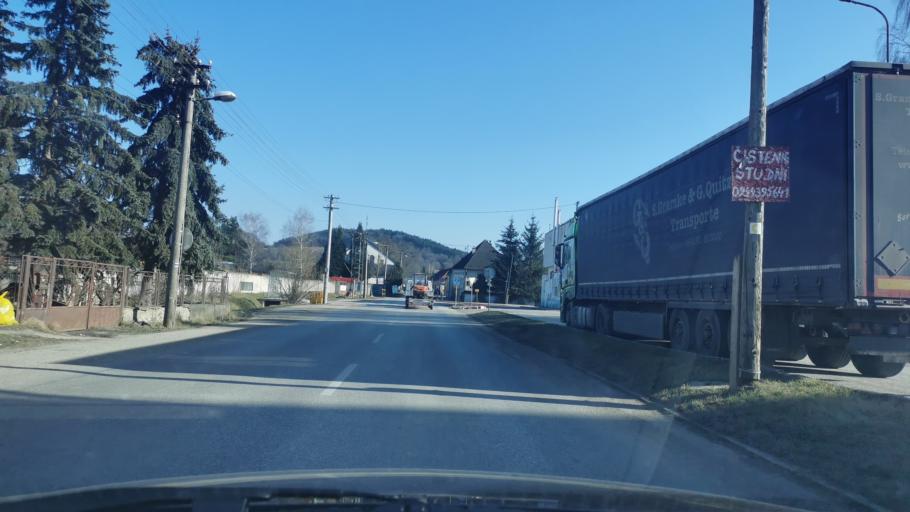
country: SK
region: Trenciansky
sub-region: Okres Myjava
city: Myjava
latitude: 48.7453
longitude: 17.5342
